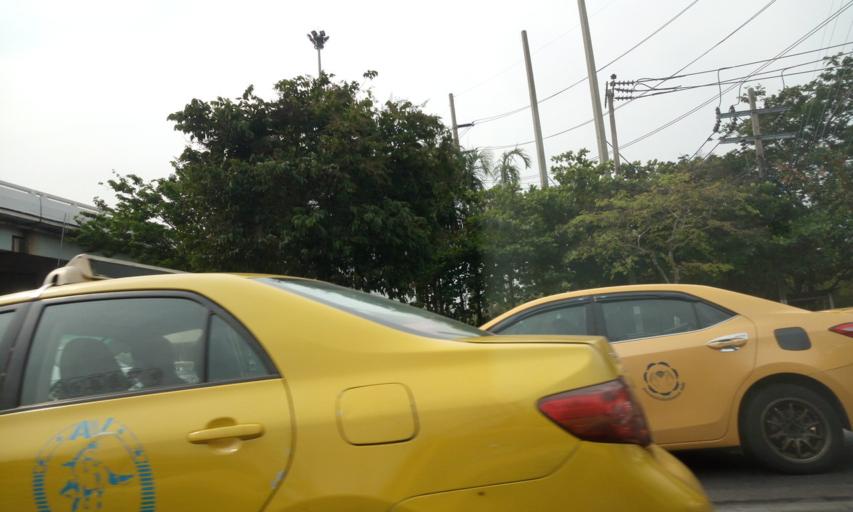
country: TH
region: Bangkok
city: Lat Krabang
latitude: 13.7226
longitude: 100.7471
